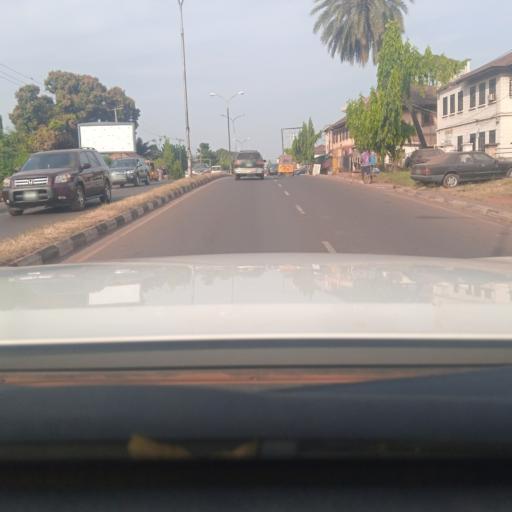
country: NG
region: Enugu
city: Enugu
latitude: 6.4481
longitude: 7.5002
